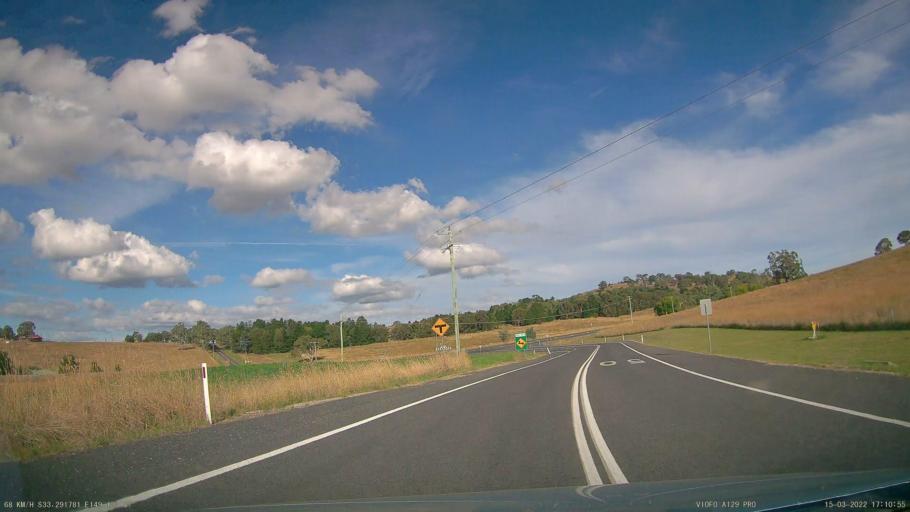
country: AU
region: New South Wales
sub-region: Orange Municipality
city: Orange
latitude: -33.2919
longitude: 149.1334
